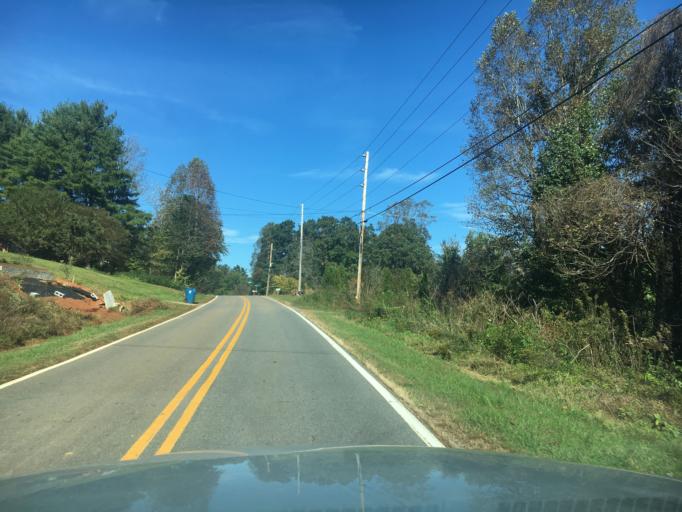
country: US
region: North Carolina
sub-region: Burke County
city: Salem
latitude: 35.7087
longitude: -81.7352
